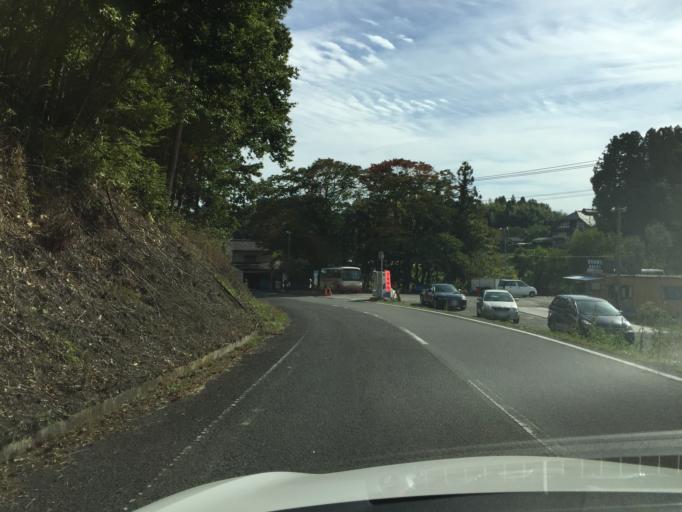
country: JP
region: Fukushima
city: Nihommatsu
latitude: 37.5811
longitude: 140.4705
